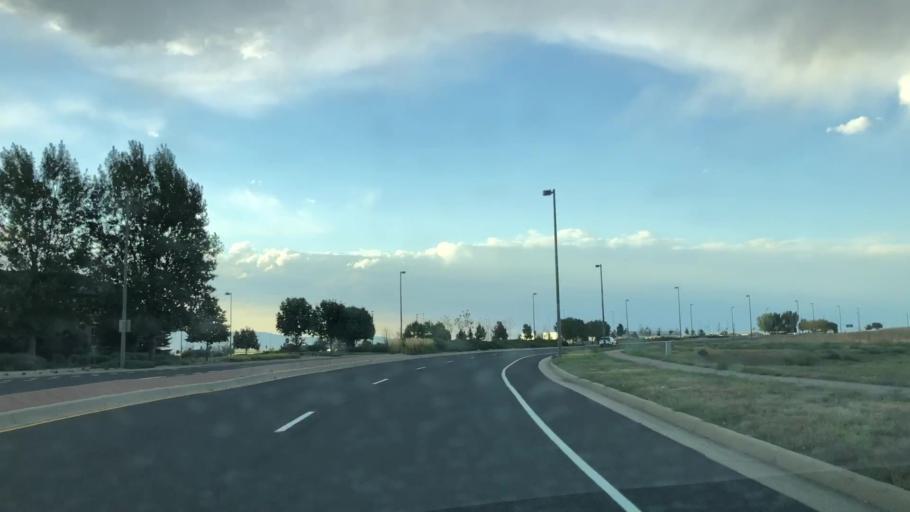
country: US
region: Colorado
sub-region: Larimer County
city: Loveland
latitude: 40.4208
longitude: -104.9978
